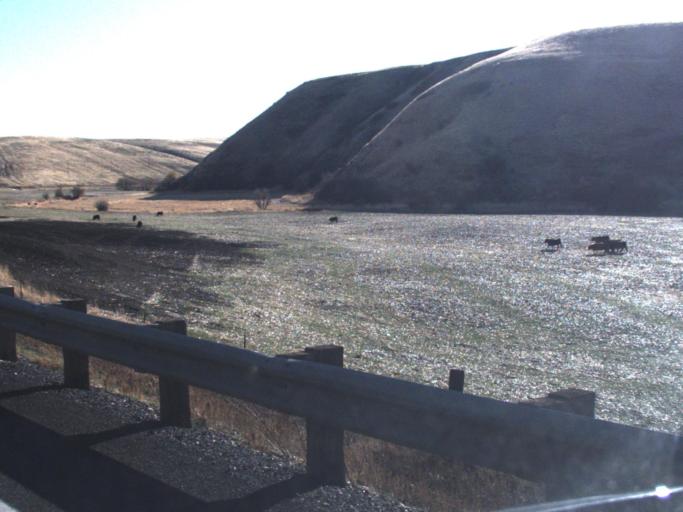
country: US
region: Washington
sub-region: Garfield County
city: Pomeroy
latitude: 46.4681
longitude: -117.4877
